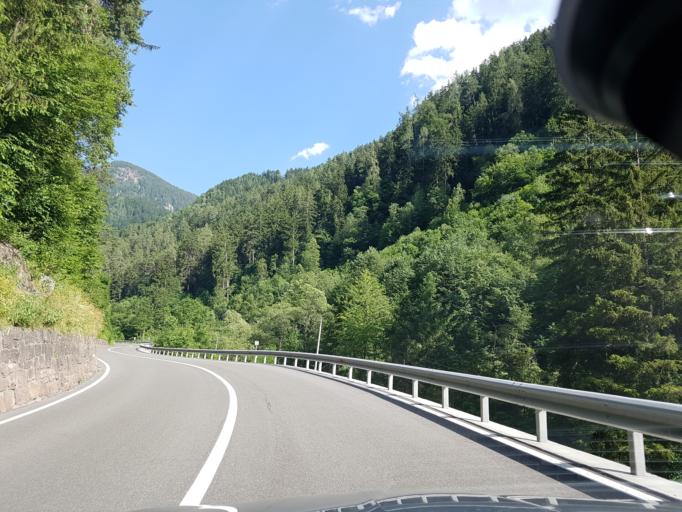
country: IT
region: Trentino-Alto Adige
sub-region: Bolzano
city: Laion
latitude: 46.5959
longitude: 11.5708
